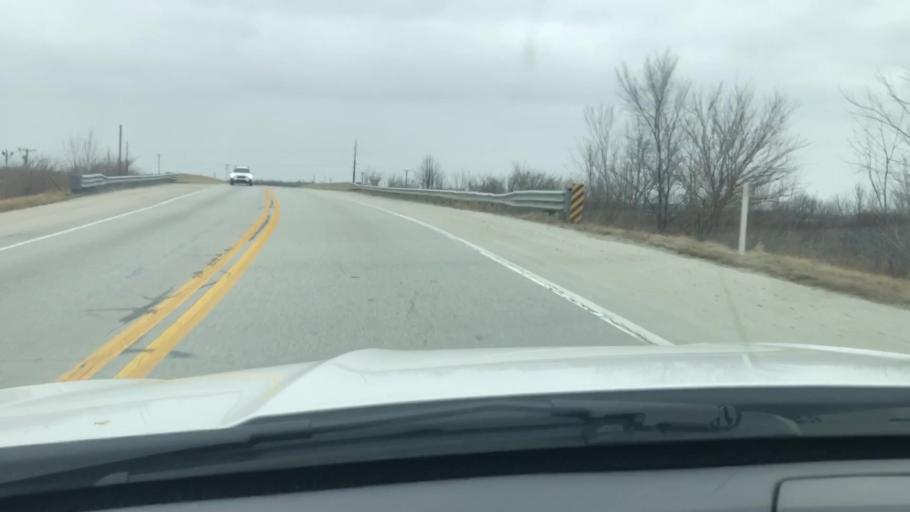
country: US
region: Indiana
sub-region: Tippecanoe County
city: Dayton
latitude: 40.3732
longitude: -86.8141
